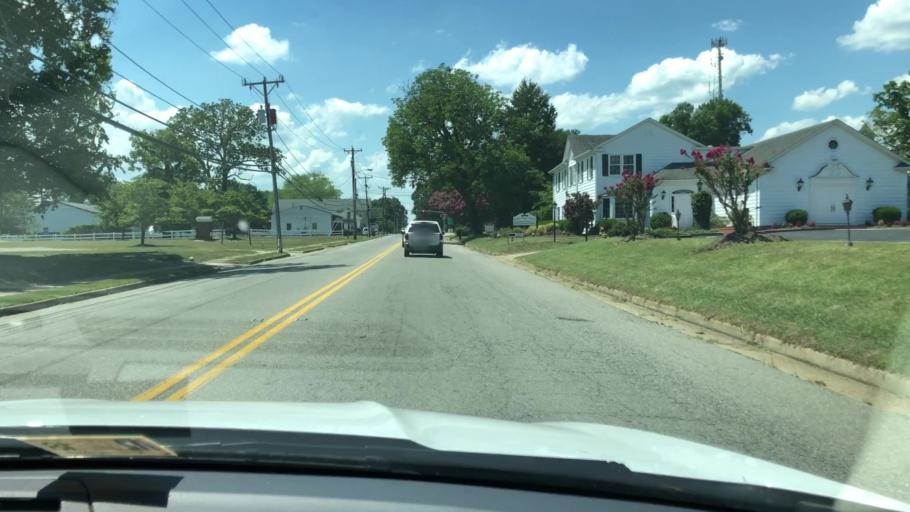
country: US
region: Virginia
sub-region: Middlesex County
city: Saluda
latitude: 37.6054
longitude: -76.5925
